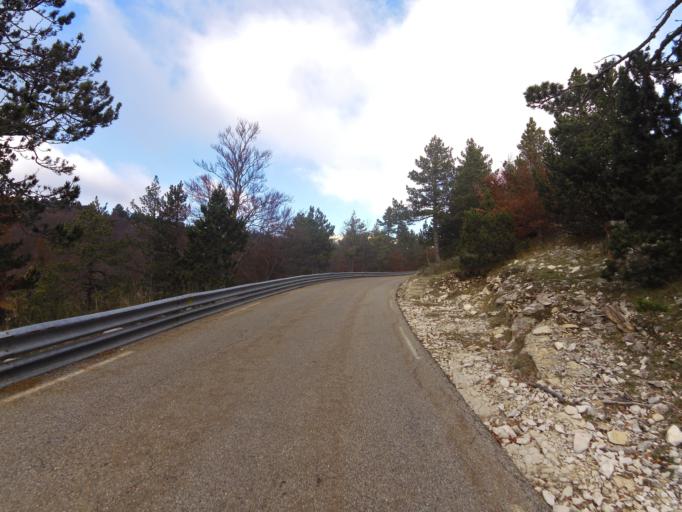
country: FR
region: Provence-Alpes-Cote d'Azur
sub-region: Departement du Vaucluse
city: Sault
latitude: 44.1467
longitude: 5.3153
